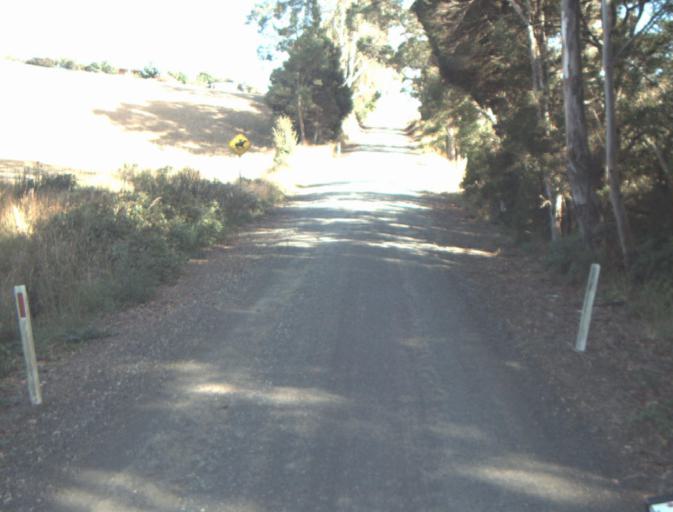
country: AU
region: Tasmania
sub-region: Dorset
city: Bridport
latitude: -41.1549
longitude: 147.2331
